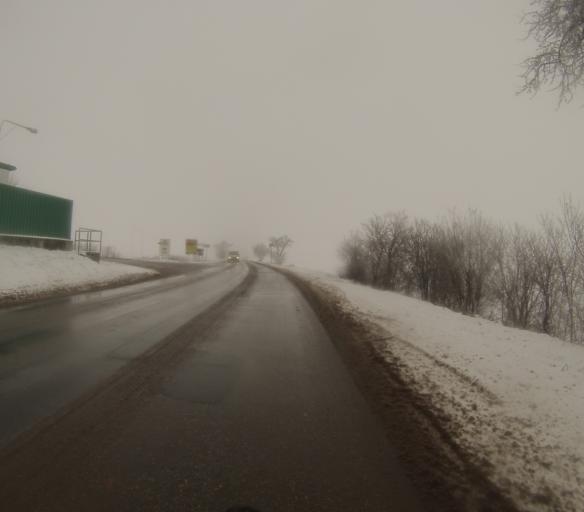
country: CZ
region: South Moravian
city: Strelice
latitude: 49.1593
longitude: 16.5057
